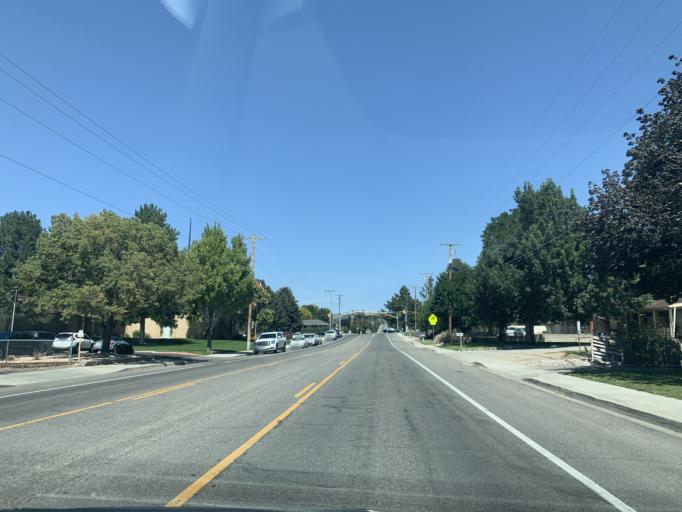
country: US
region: Utah
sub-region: Utah County
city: Lehi
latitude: 40.3974
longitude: -111.8301
